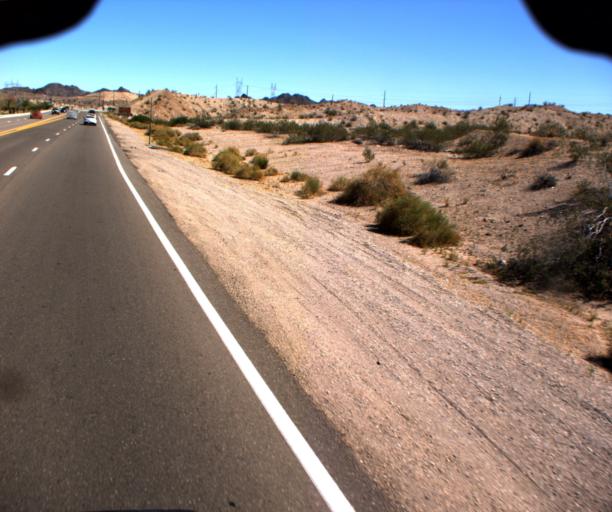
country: US
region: Nevada
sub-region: Clark County
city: Laughlin
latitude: 35.1790
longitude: -114.5646
